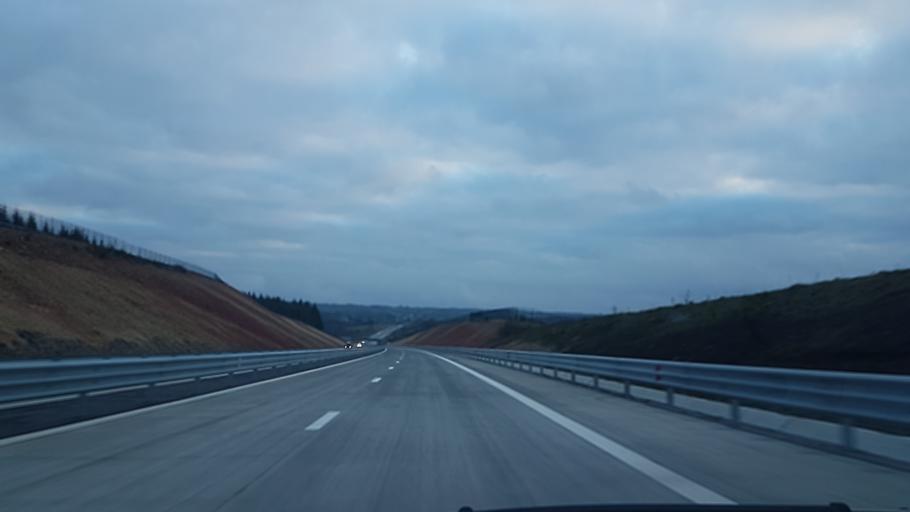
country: FR
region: Champagne-Ardenne
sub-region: Departement des Ardennes
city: Rocroi
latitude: 49.9848
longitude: 4.5397
